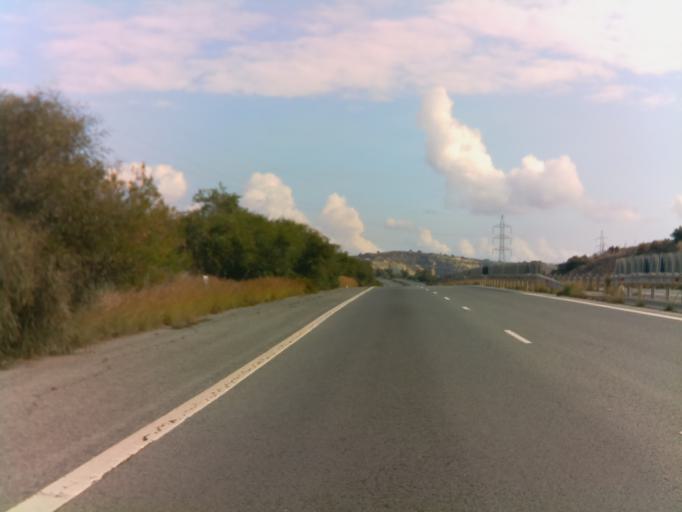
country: CY
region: Limassol
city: Pyrgos
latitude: 34.7275
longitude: 33.2757
